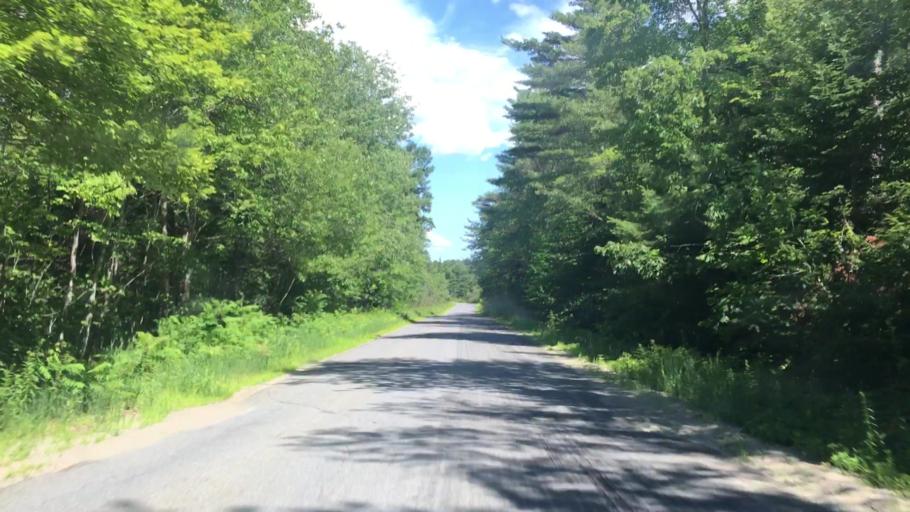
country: US
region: Maine
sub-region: Franklin County
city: Chesterville
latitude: 44.5533
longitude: -70.1013
